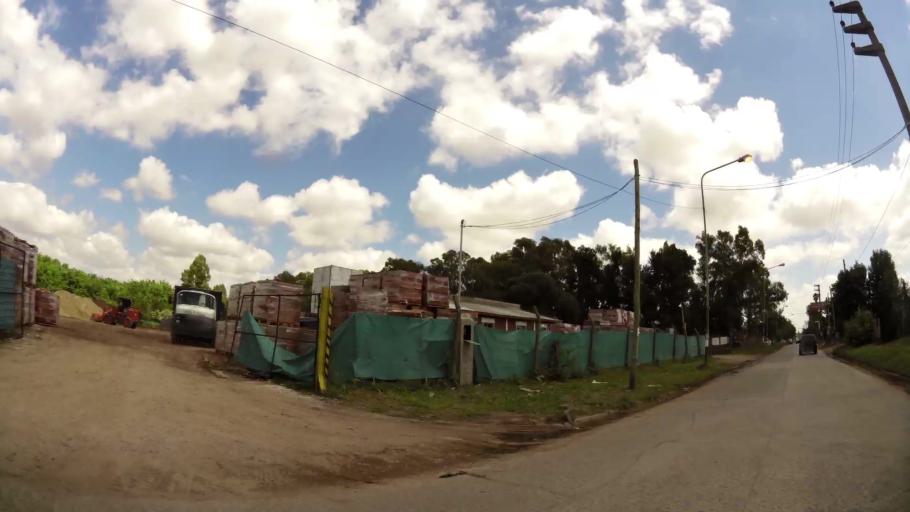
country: AR
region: Buenos Aires
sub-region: Partido de Quilmes
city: Quilmes
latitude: -34.8319
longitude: -58.2420
